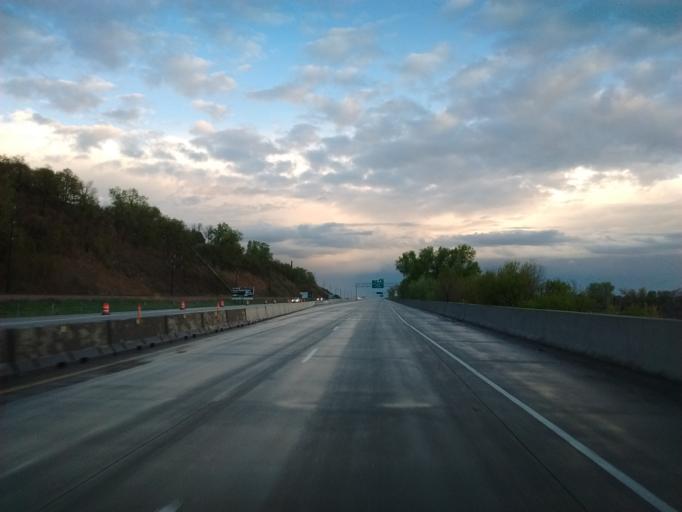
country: US
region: Nebraska
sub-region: Dakota County
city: South Sioux City
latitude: 42.4698
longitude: -96.3817
